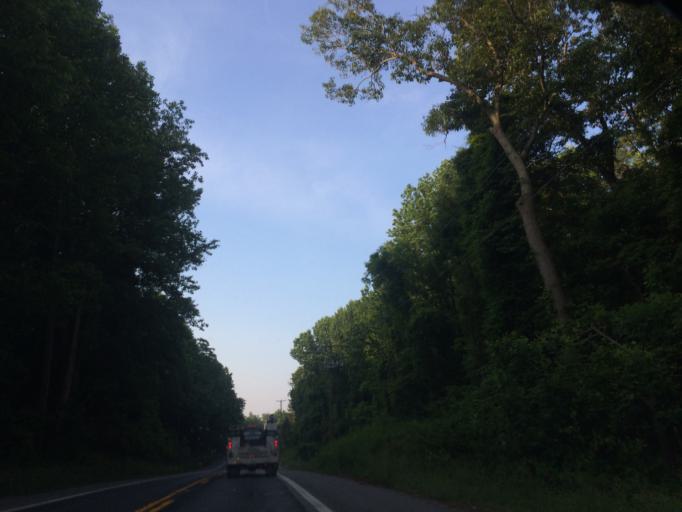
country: US
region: Maryland
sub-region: Montgomery County
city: Olney
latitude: 39.2490
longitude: -77.0552
